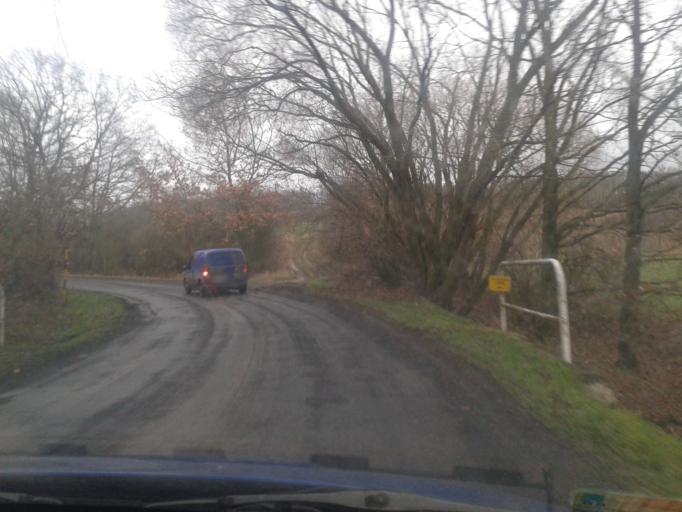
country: CZ
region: Central Bohemia
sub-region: Okres Beroun
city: Beroun
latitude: 49.8949
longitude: 14.1394
